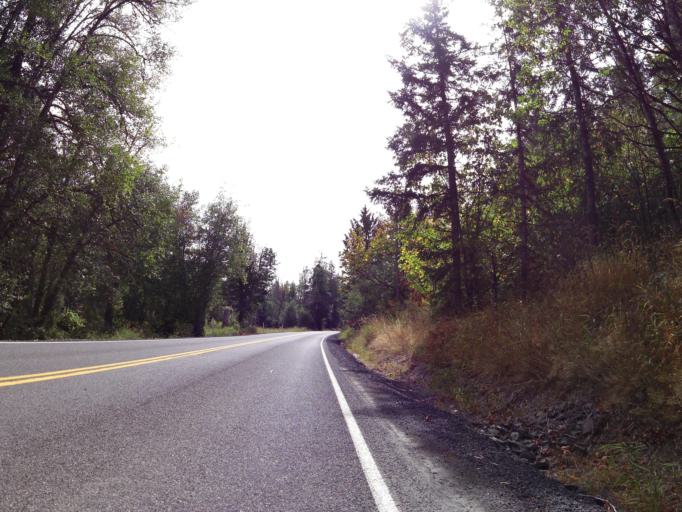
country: US
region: Washington
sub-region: Lewis County
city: Napavine
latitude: 46.5510
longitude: -122.9556
